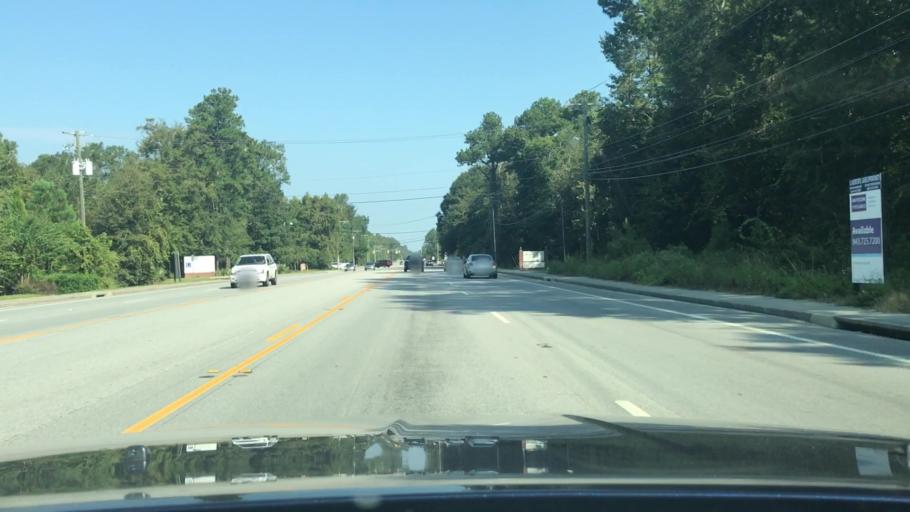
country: US
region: South Carolina
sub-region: Dorchester County
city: Centerville
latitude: 32.9687
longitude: -80.1684
